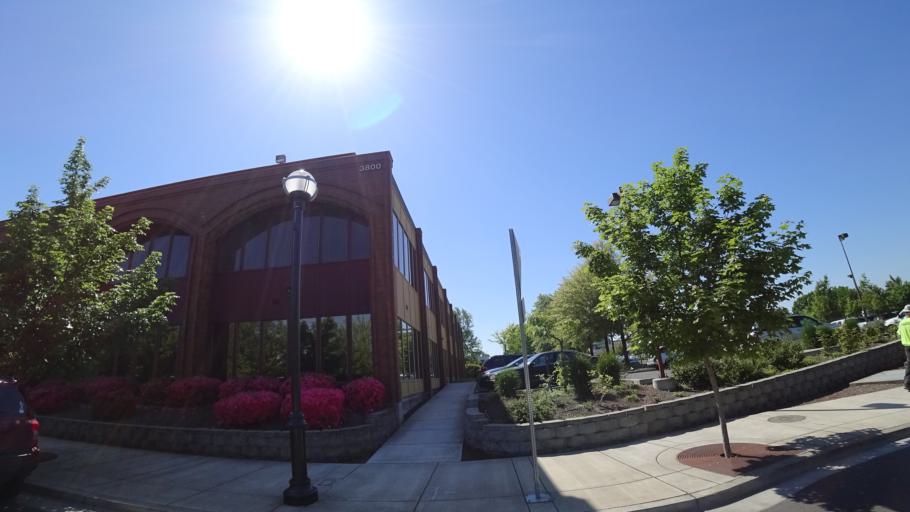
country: US
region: Oregon
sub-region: Washington County
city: Beaverton
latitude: 45.4922
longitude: -122.8082
